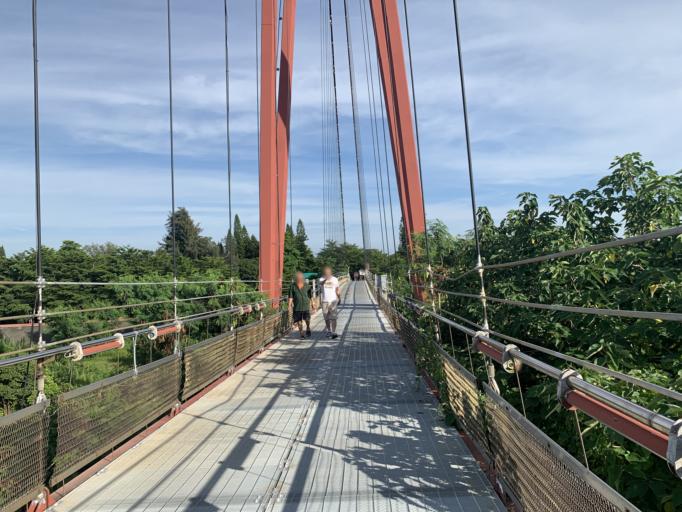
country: TW
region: Taiwan
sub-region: Chiayi
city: Taibao
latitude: 23.4822
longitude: 120.2960
